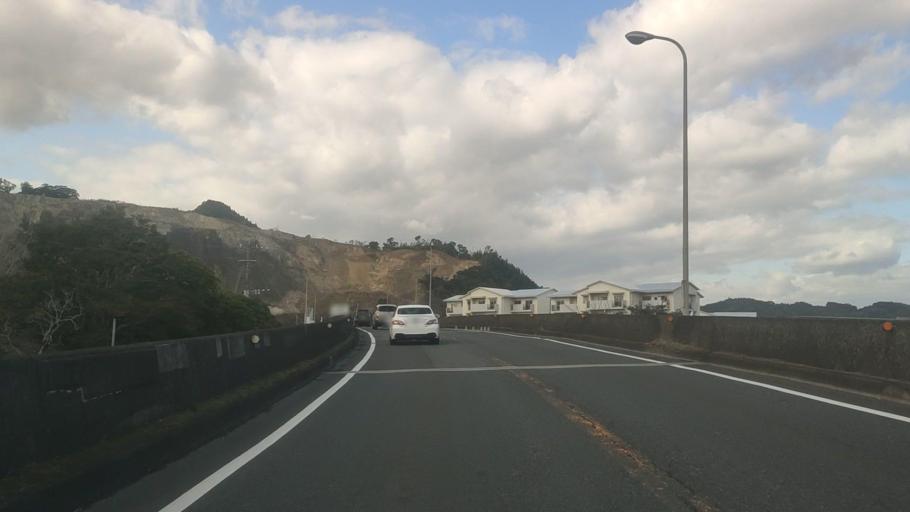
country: JP
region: Kagoshima
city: Kajiki
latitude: 31.7358
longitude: 130.6533
